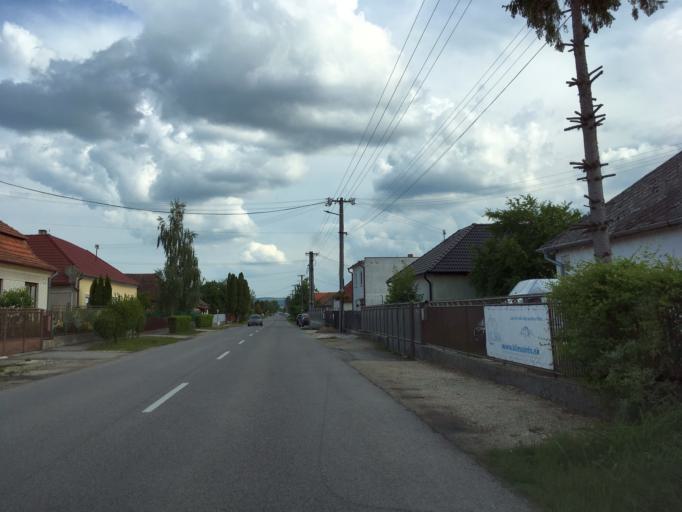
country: HU
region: Komarom-Esztergom
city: Dunaalmas
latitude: 47.7808
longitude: 18.2962
